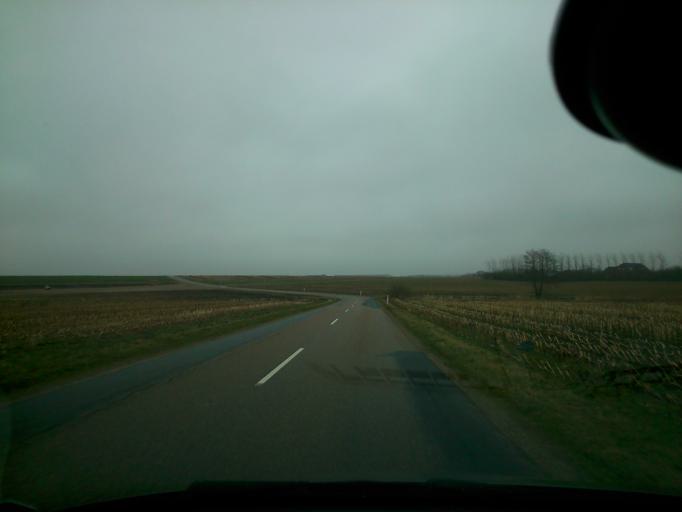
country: DK
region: Central Jutland
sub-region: Ringkobing-Skjern Kommune
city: Ringkobing
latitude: 56.0915
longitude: 8.4027
